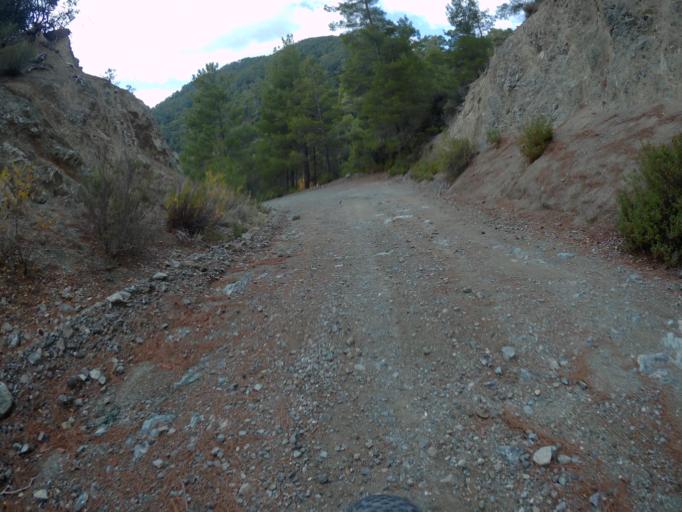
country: CY
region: Lefkosia
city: Kakopetria
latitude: 34.9059
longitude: 32.8422
